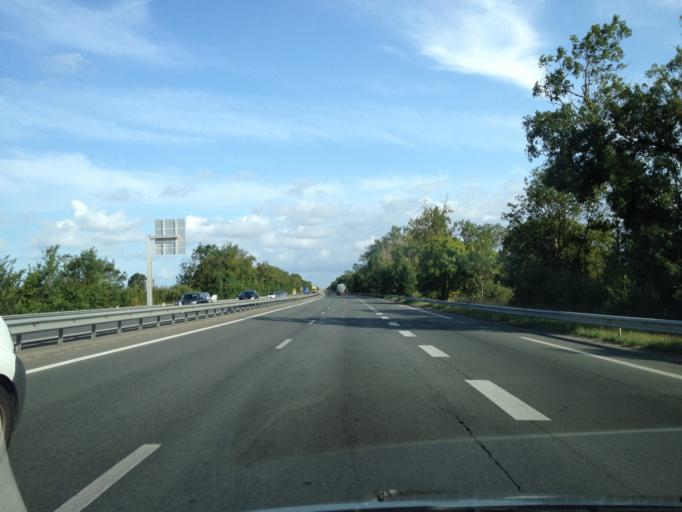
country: FR
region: Poitou-Charentes
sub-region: Departement de la Charente-Maritime
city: Chatelaillon-Plage
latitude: 46.0827
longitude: -1.0781
